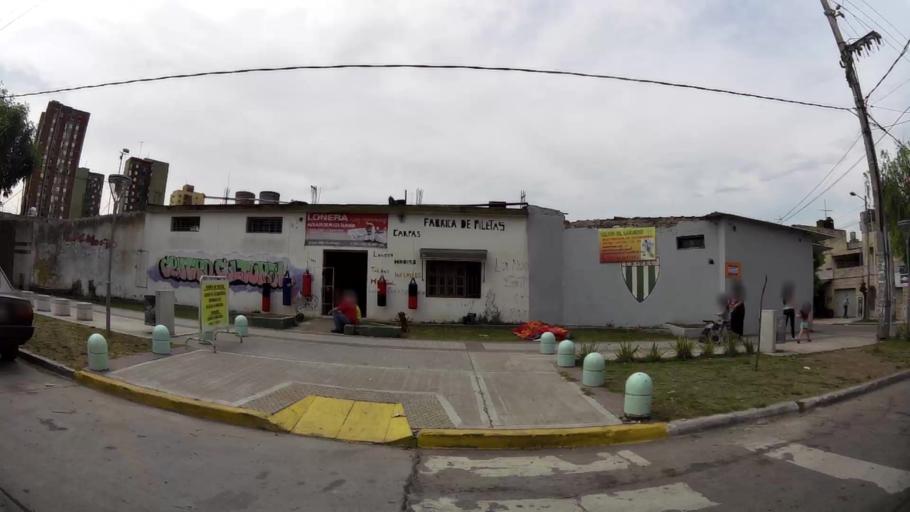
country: AR
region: Buenos Aires F.D.
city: Villa Lugano
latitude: -34.6851
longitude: -58.4928
